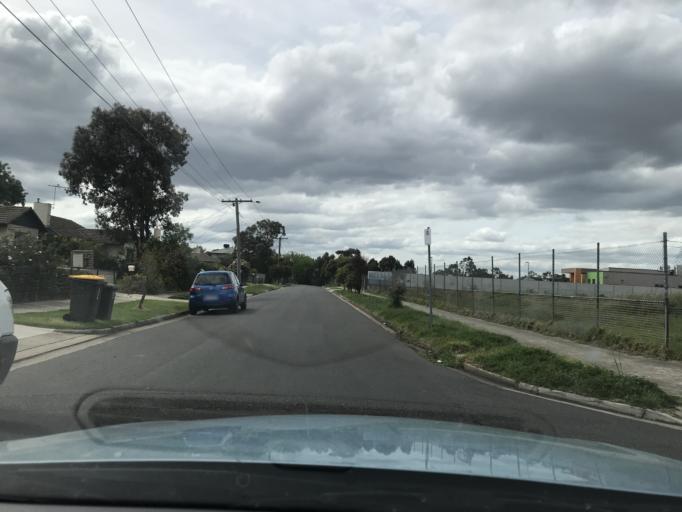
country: AU
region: Victoria
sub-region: Hobsons Bay
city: Laverton
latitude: -37.8606
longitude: 144.7712
